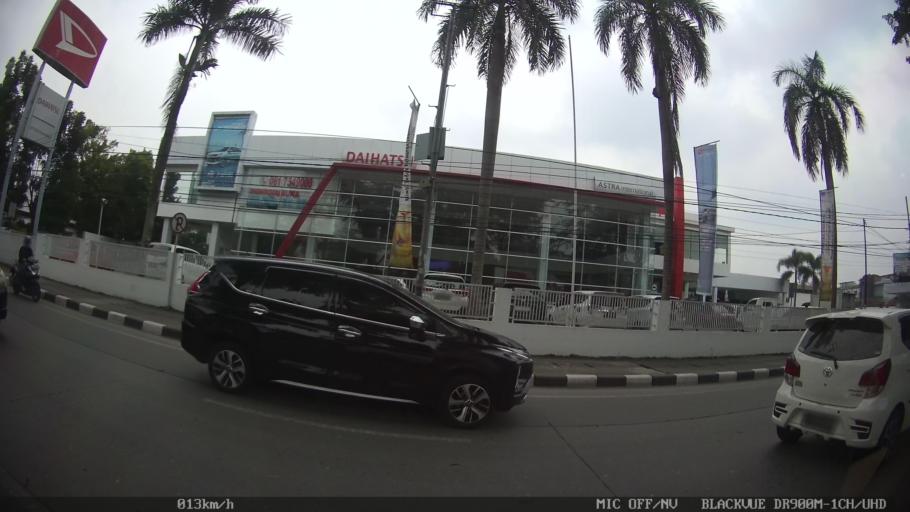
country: ID
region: North Sumatra
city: Medan
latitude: 3.5710
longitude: 98.6897
